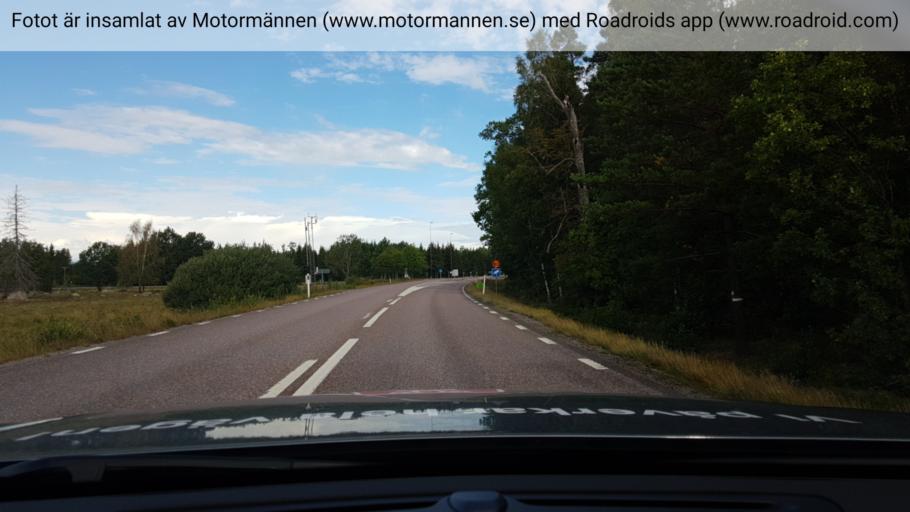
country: SE
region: Gaevleborg
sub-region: Gavle Kommun
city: Hedesunda
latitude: 60.2947
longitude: 16.9175
